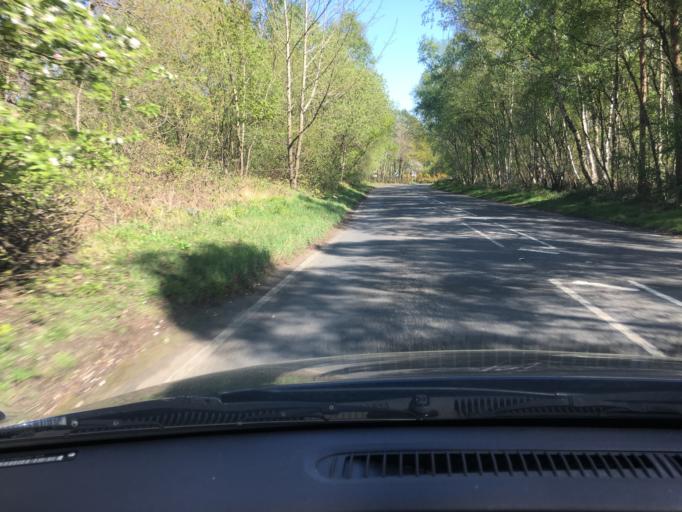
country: GB
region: England
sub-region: Hampshire
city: Yateley
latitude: 51.3246
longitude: -0.8273
